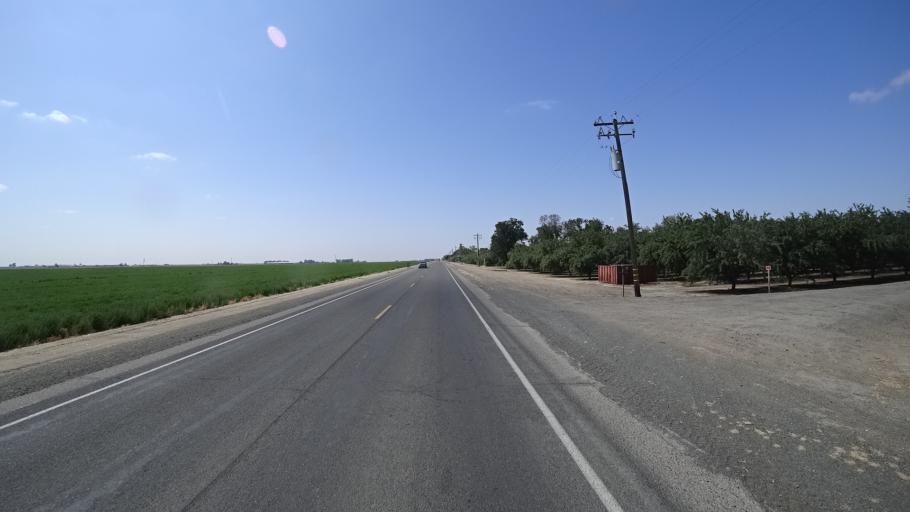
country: US
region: California
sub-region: Kings County
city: Home Garden
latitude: 36.2441
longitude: -119.6369
